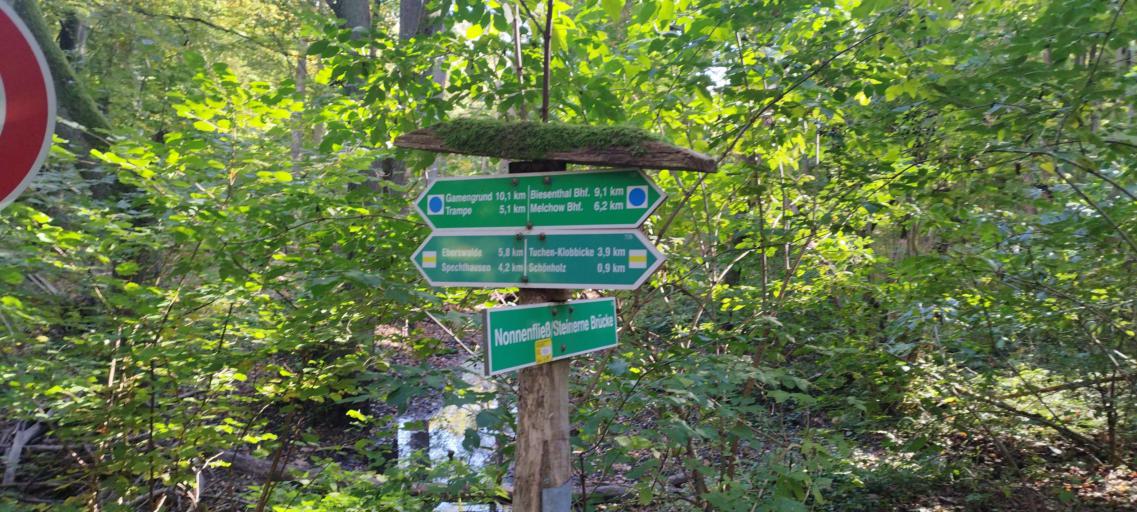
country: DE
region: Brandenburg
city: Eberswalde
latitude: 52.7833
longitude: 13.7777
